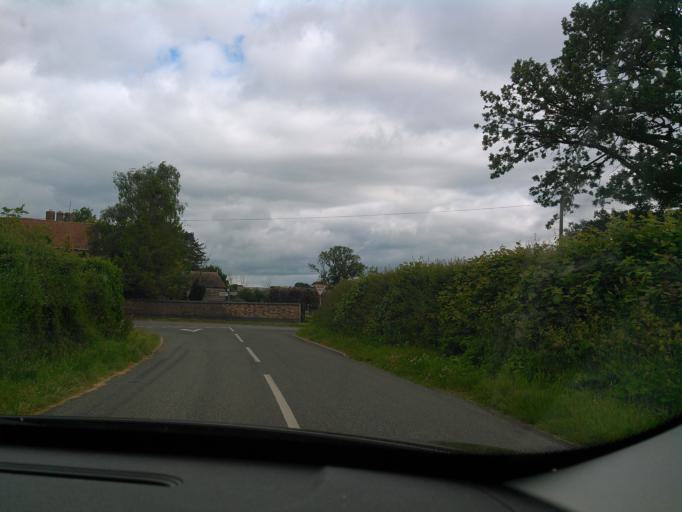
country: GB
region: England
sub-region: Shropshire
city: Wem
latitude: 52.8699
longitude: -2.7423
